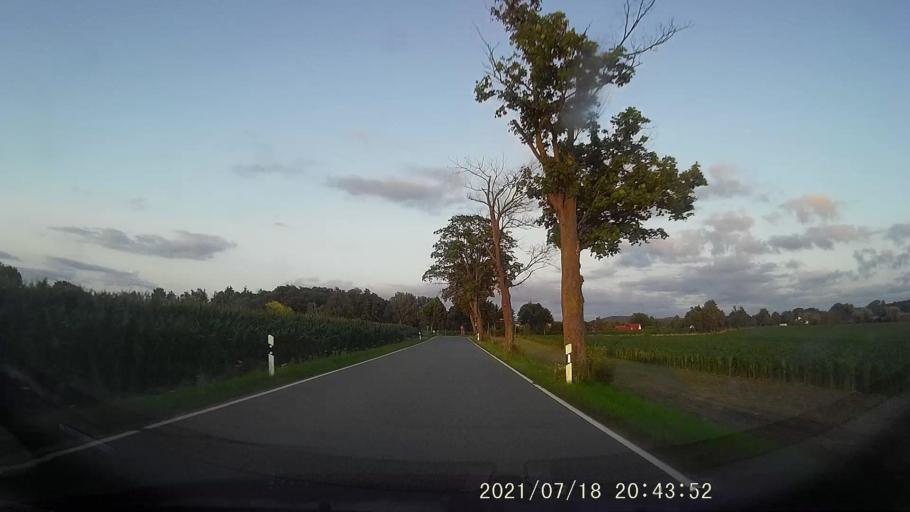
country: DE
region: Saxony
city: Reichenbach
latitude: 51.2018
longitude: 14.7705
